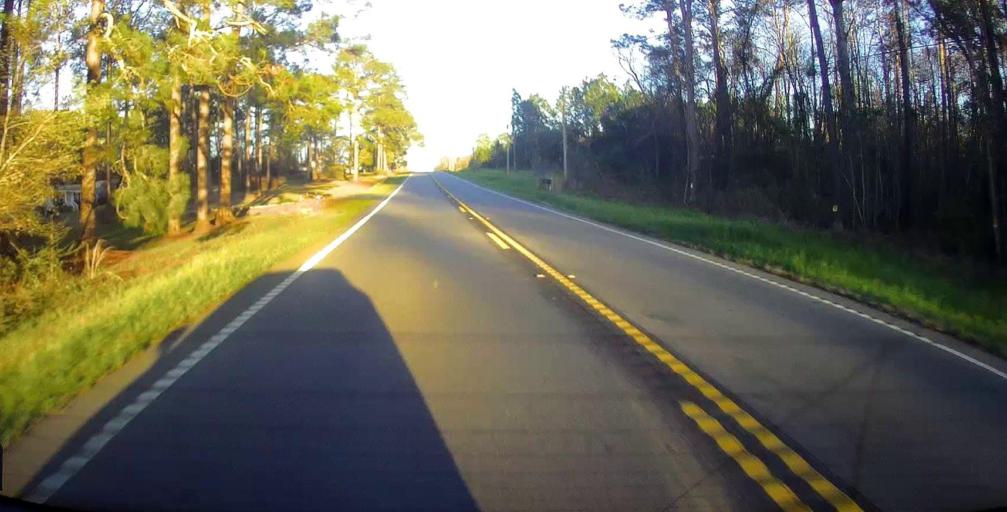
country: US
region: Georgia
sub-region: Crisp County
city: Cordele
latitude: 31.9574
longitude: -83.6699
